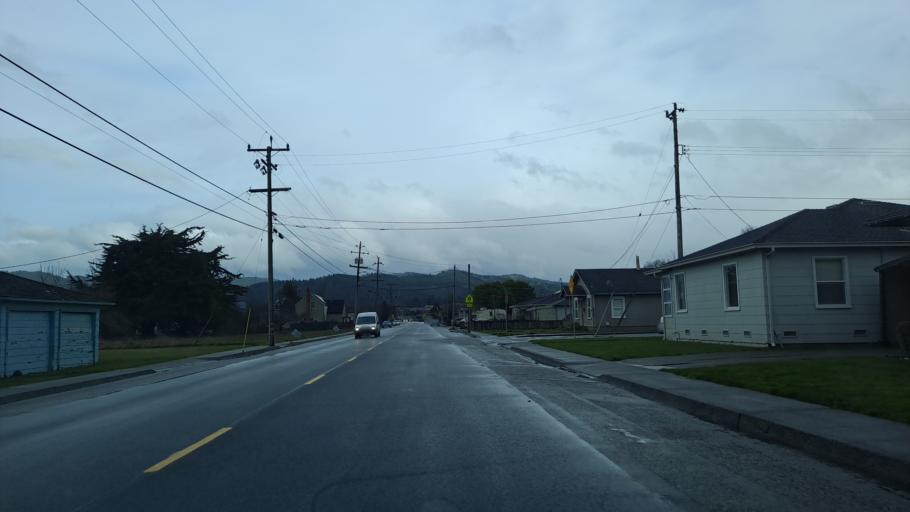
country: US
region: California
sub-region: Humboldt County
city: Fortuna
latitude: 40.5885
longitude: -124.1502
